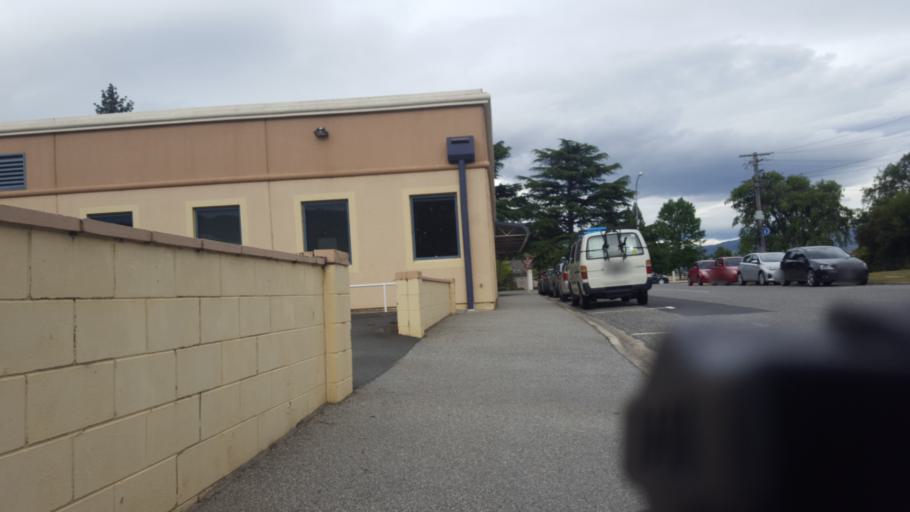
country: NZ
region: Otago
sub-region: Queenstown-Lakes District
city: Wanaka
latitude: -45.2548
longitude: 169.3944
